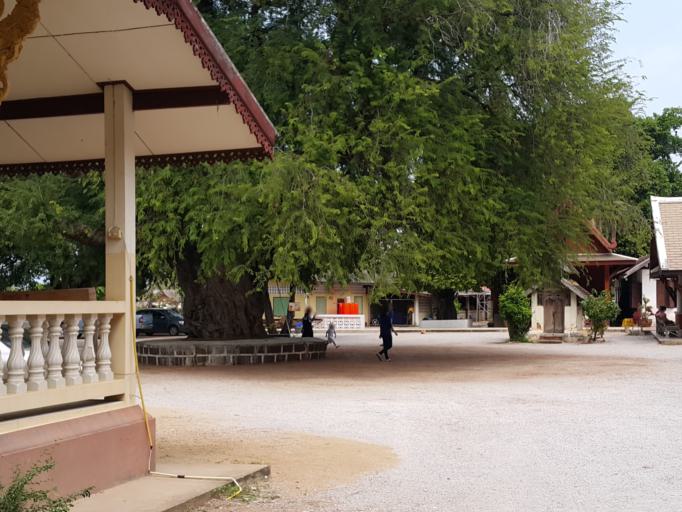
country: TH
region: Lampang
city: Ko Kha
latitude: 18.2166
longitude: 99.3880
